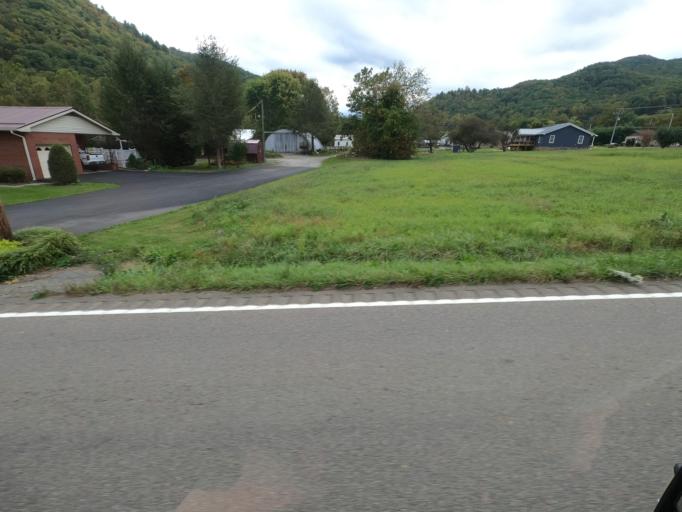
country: US
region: Tennessee
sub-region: Carter County
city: Elizabethton
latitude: 36.2619
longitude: -82.1891
